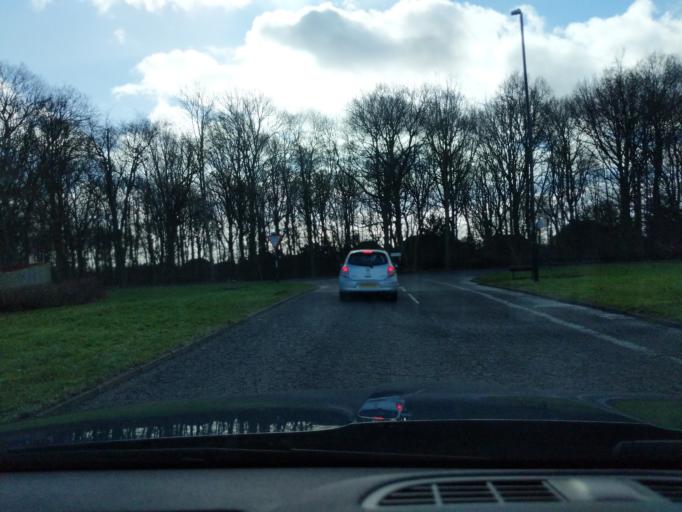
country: GB
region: England
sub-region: Sunderland
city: Washington
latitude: 54.8785
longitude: -1.5415
